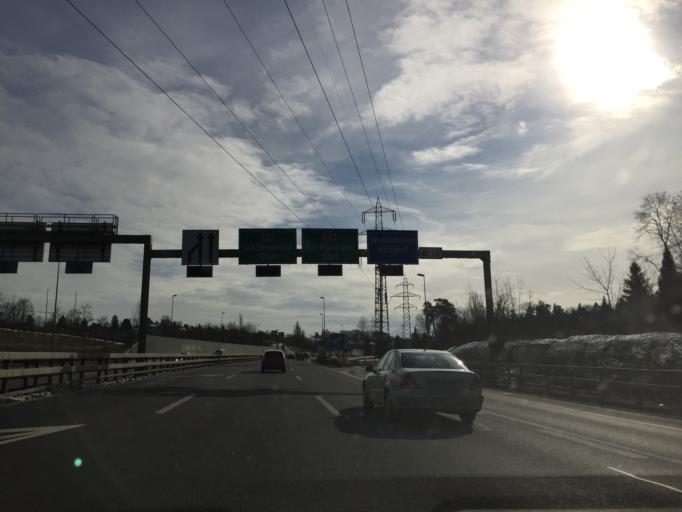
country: CH
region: Zurich
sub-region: Bezirk Zuerich
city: Zuerich (Kreis 2)
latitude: 47.3311
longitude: 8.5279
